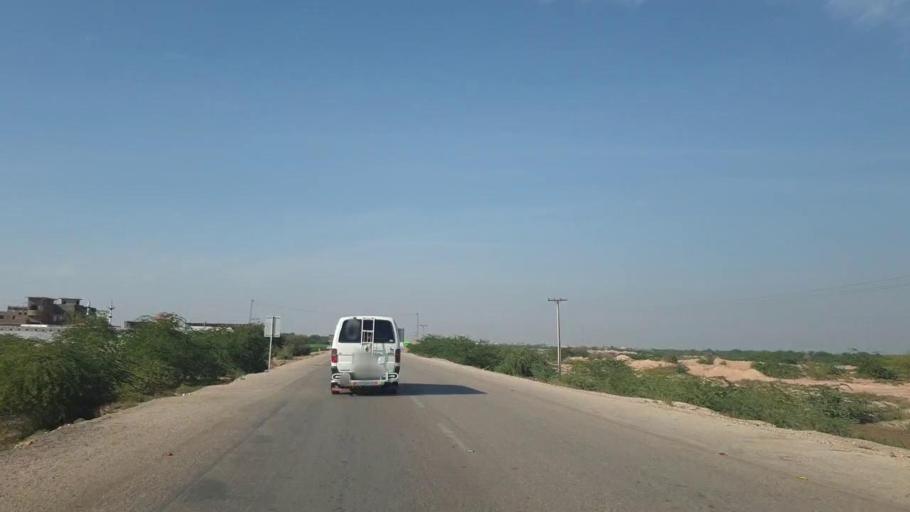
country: PK
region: Sindh
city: Sehwan
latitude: 26.3872
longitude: 67.8701
